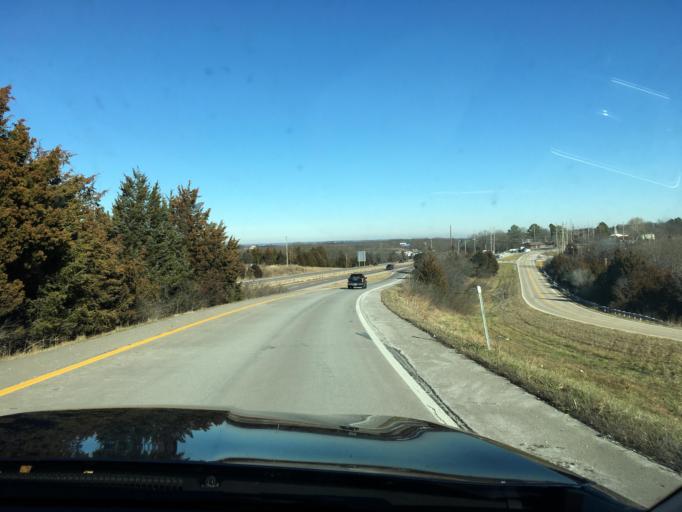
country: US
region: Missouri
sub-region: Jefferson County
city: De Soto
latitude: 38.1372
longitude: -90.4707
